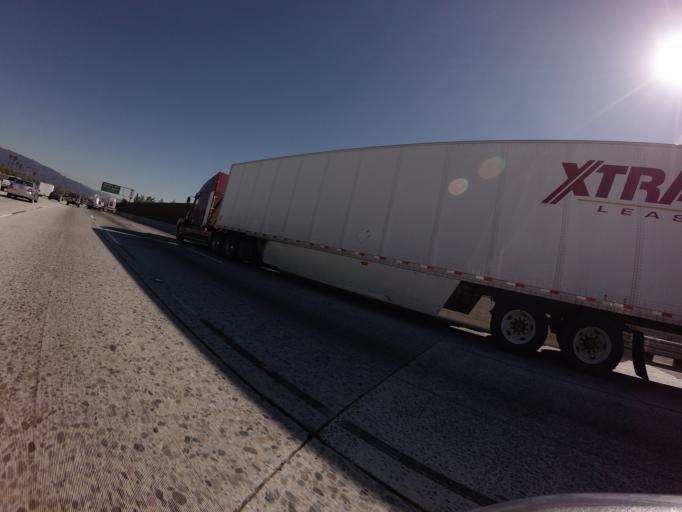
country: US
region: California
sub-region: Los Angeles County
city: Monrovia
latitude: 34.1361
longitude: -118.0090
